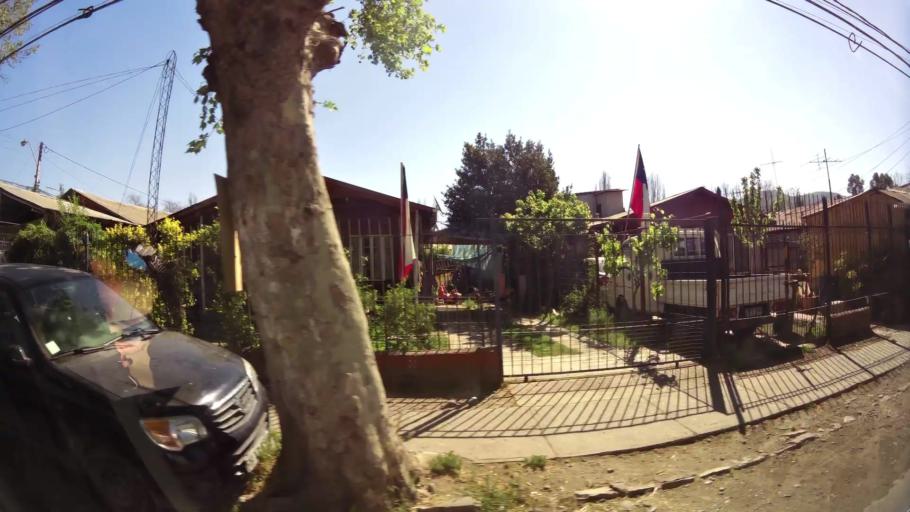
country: CL
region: Santiago Metropolitan
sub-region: Provincia de Talagante
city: Penaflor
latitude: -33.6036
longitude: -70.8953
